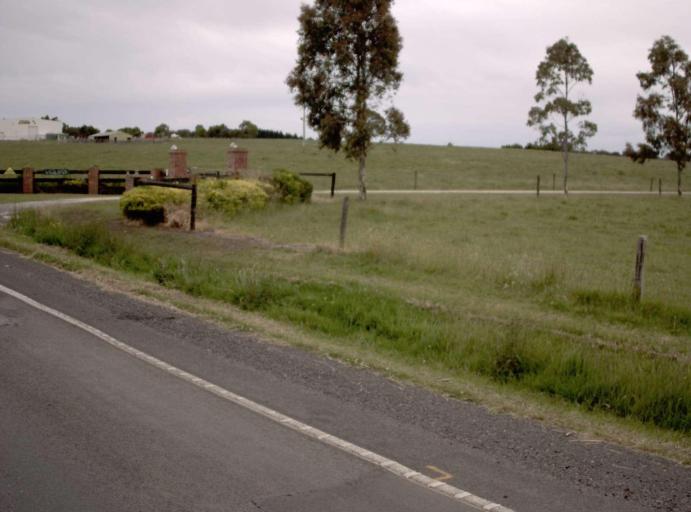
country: AU
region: Victoria
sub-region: Bass Coast
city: North Wonthaggi
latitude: -38.5281
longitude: 145.9518
